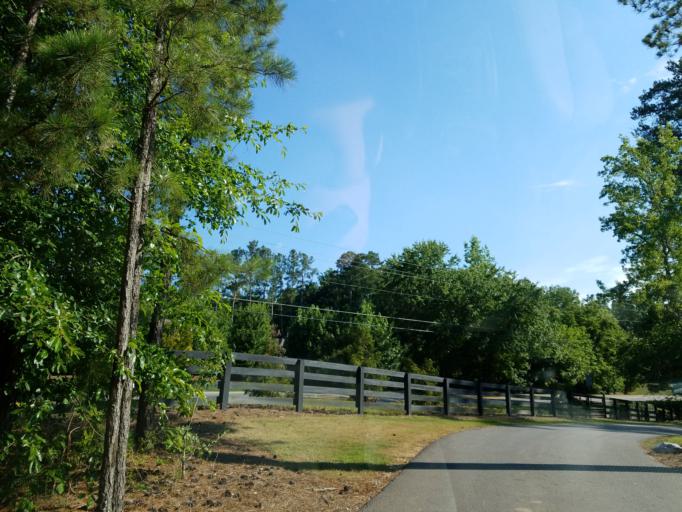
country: US
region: Georgia
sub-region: Fulton County
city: Milton
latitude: 34.1839
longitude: -84.3197
